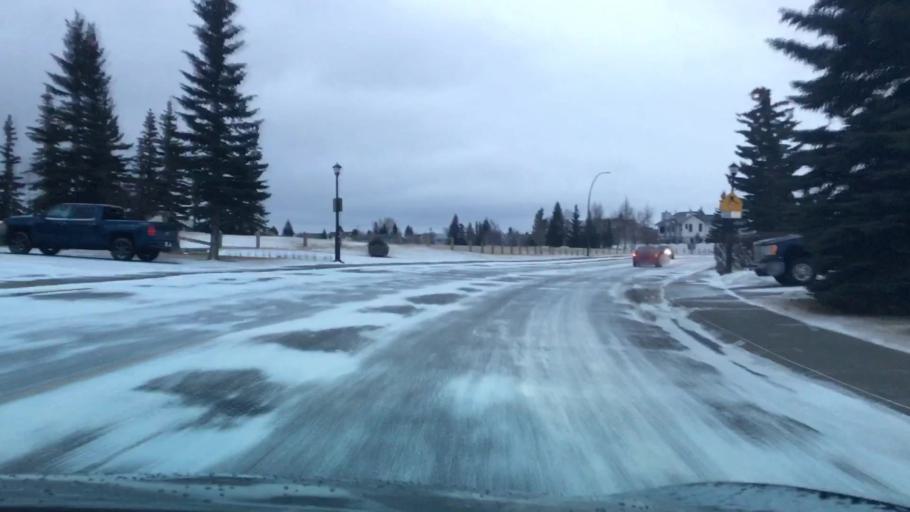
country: CA
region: Alberta
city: Calgary
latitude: 51.1327
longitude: -114.1662
